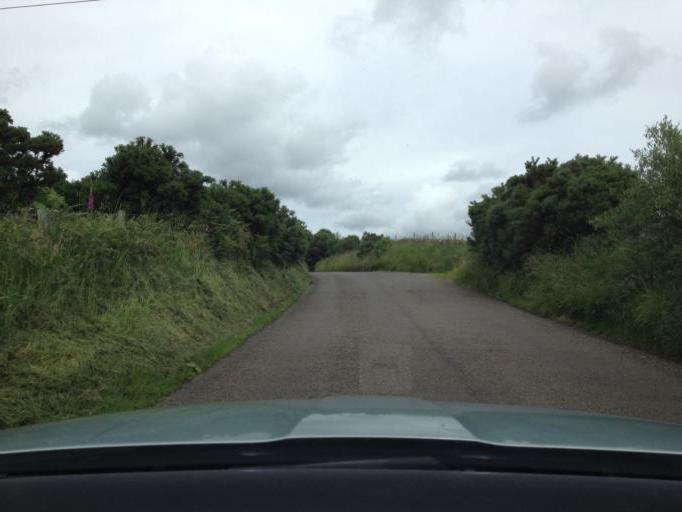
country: GB
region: Scotland
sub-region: Angus
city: Brechin
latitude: 56.8475
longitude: -2.6756
